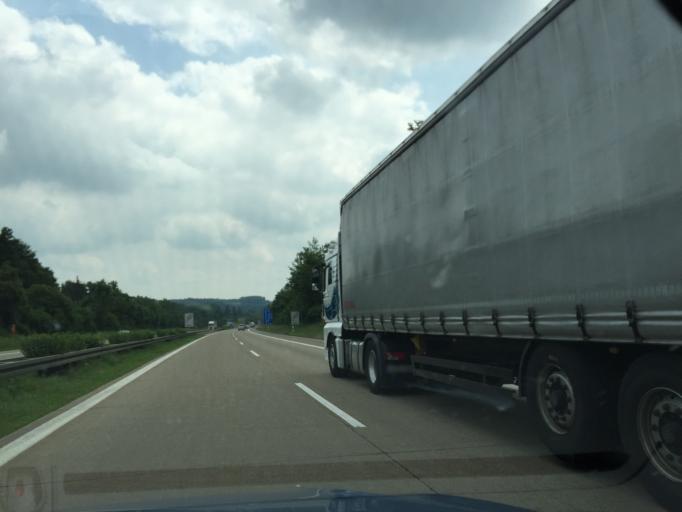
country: DE
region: Baden-Wuerttemberg
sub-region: Regierungsbezirk Stuttgart
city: Nattheim
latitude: 48.7038
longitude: 10.2147
